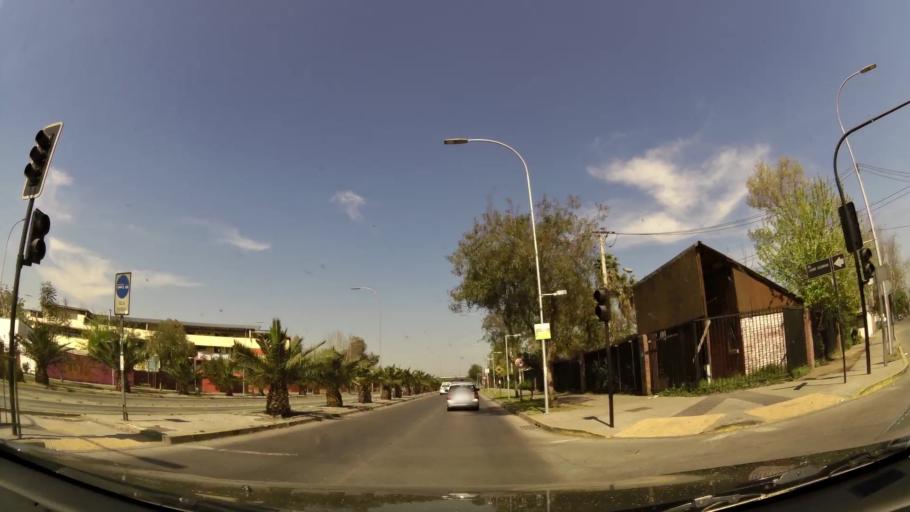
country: CL
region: Santiago Metropolitan
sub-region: Provincia de Santiago
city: Lo Prado
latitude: -33.4034
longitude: -70.7031
